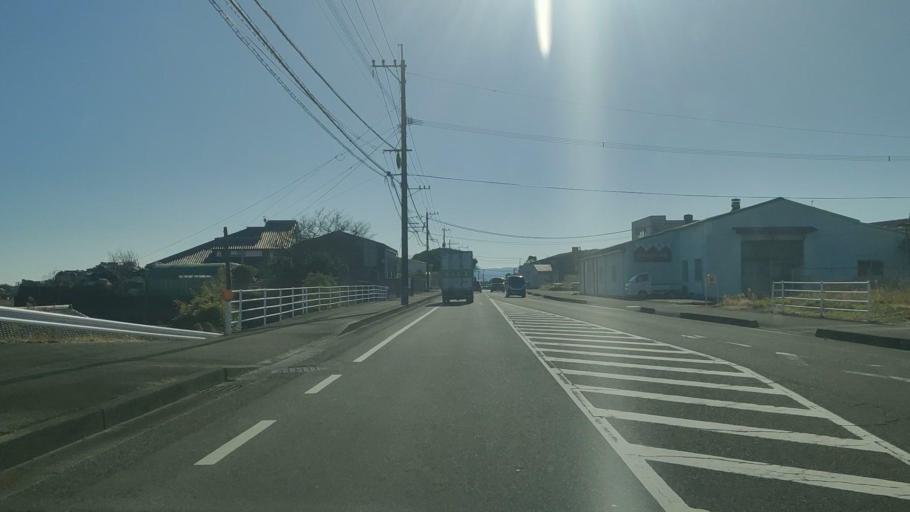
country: JP
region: Miyazaki
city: Miyazaki-shi
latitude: 31.9465
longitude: 131.4591
